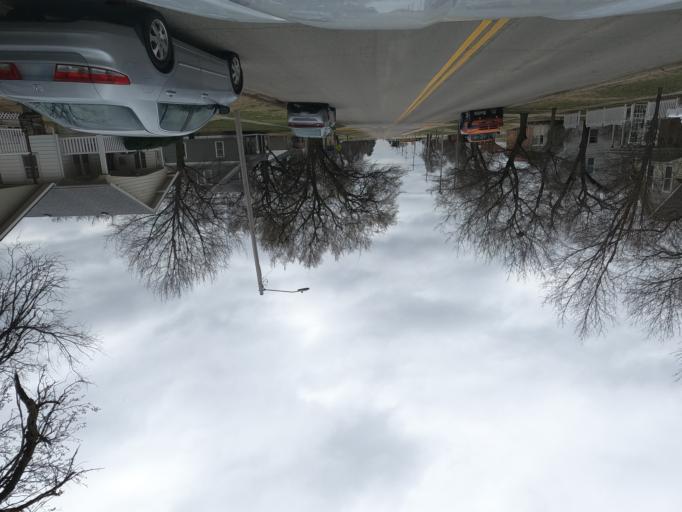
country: US
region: Kansas
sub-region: McPherson County
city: Inman
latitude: 38.2291
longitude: -97.7758
